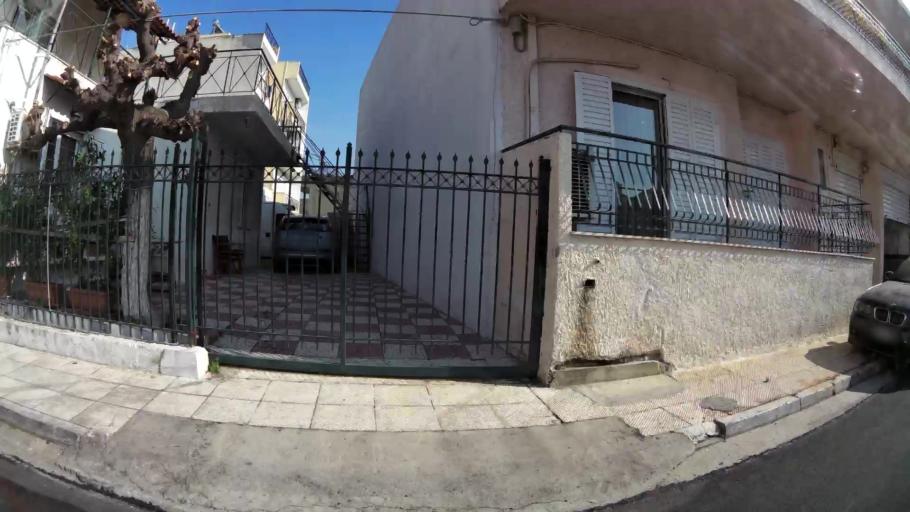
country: GR
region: Attica
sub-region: Nomarchia Dytikis Attikis
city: Zefyri
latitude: 38.0745
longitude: 23.7179
